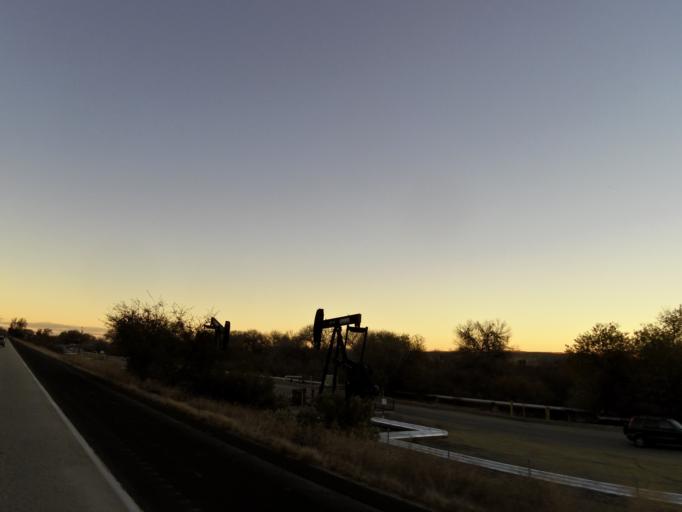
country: US
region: California
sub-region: San Luis Obispo County
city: Lake Nacimiento
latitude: 35.9567
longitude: -120.8819
